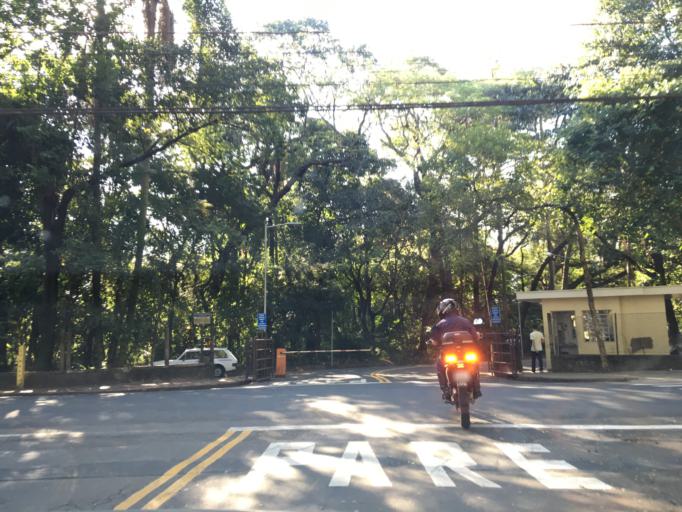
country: BR
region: Sao Paulo
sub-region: Piracicaba
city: Piracicaba
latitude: -22.7120
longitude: -47.6316
